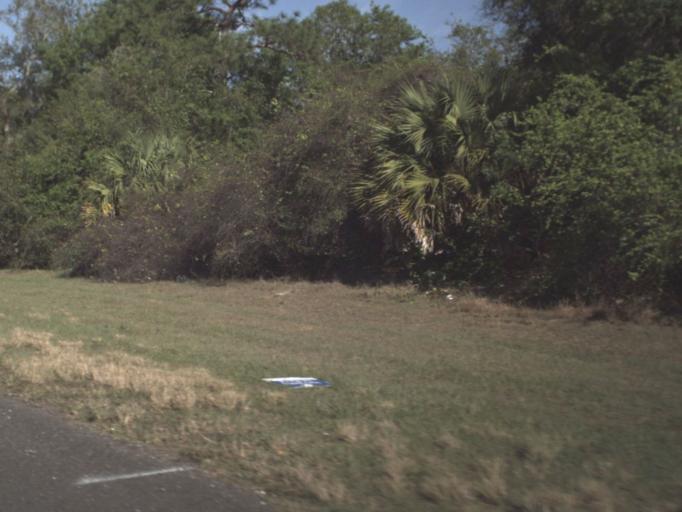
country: US
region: Florida
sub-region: Lake County
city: Howie In The Hills
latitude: 28.6411
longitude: -81.7986
